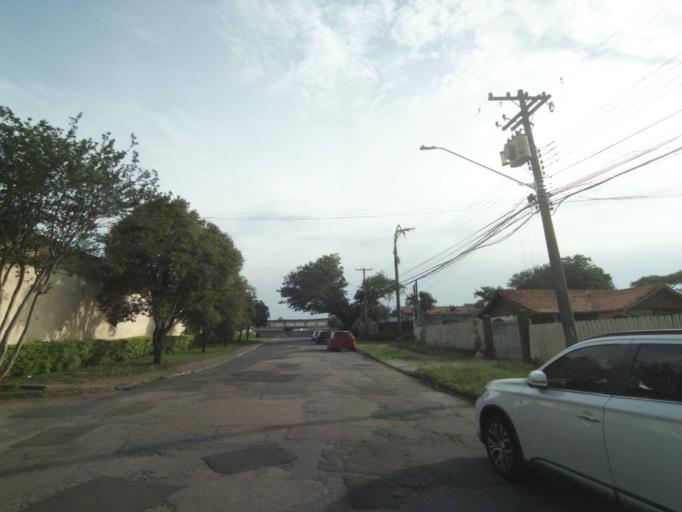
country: BR
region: Parana
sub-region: Pinhais
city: Pinhais
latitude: -25.4312
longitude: -49.2311
